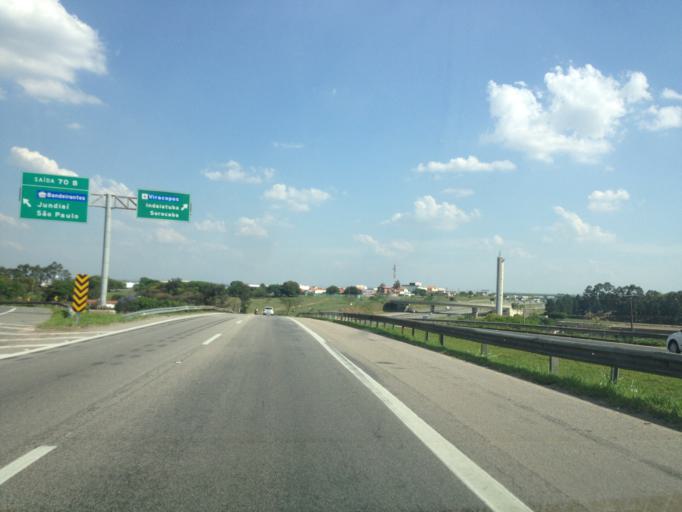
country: BR
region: Sao Paulo
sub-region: Campinas
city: Campinas
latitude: -22.9942
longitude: -47.1104
